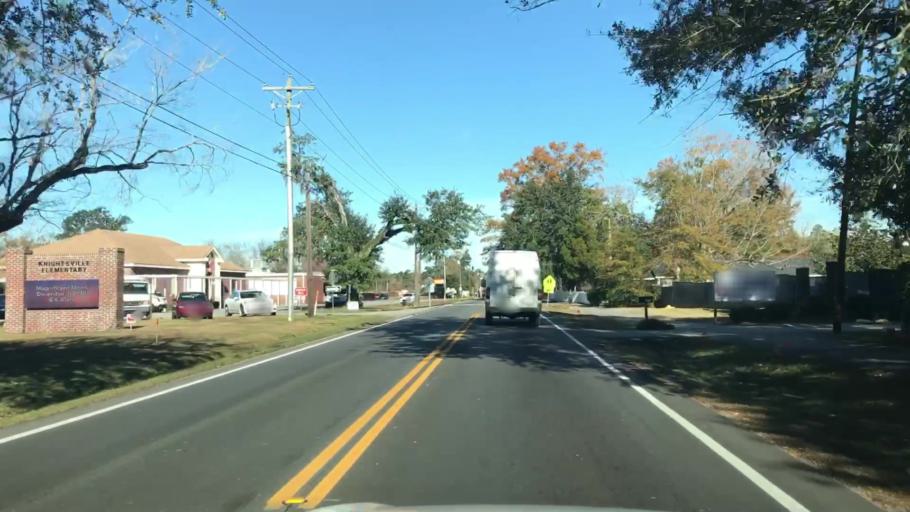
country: US
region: South Carolina
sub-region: Dorchester County
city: Summerville
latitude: 33.0078
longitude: -80.2362
